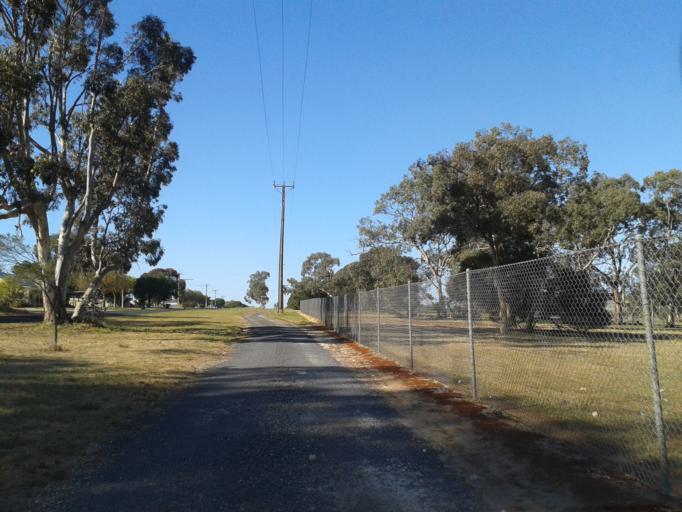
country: AU
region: South Australia
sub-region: Tatiara
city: Bordertown
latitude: -36.3093
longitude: 140.7823
